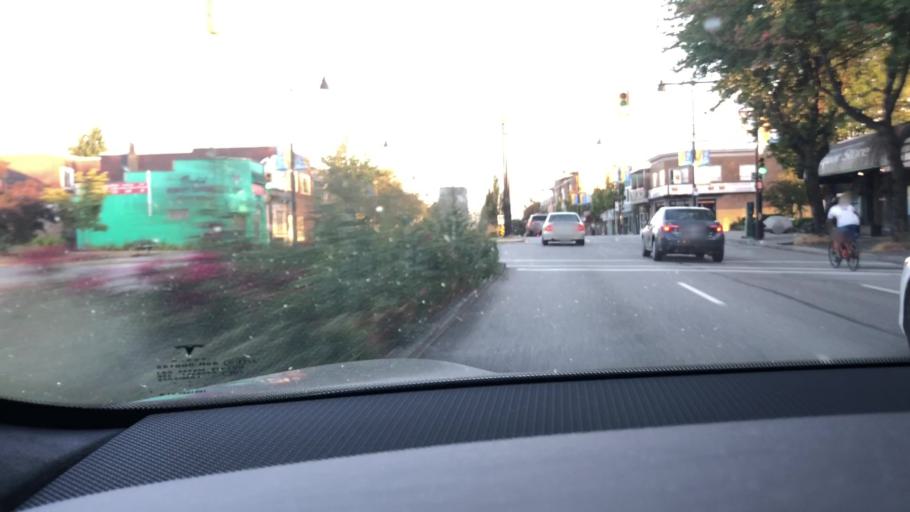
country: CA
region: British Columbia
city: Vancouver
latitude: 49.2510
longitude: -123.0776
